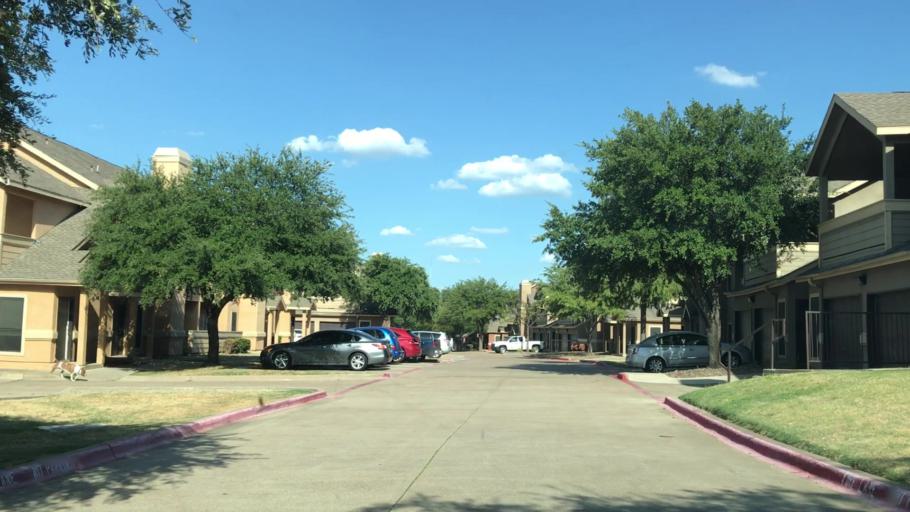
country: US
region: Texas
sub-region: Dallas County
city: Coppell
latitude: 32.9456
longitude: -96.9574
